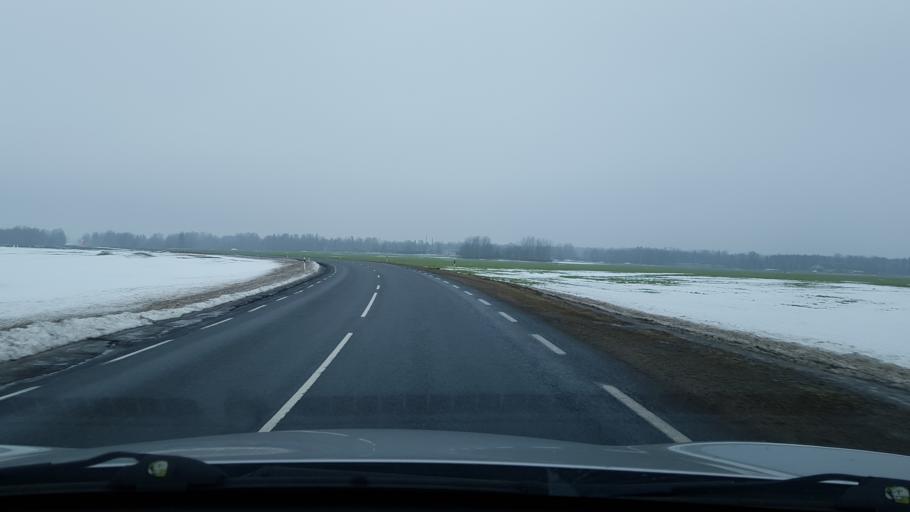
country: EE
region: Valgamaa
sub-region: Torva linn
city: Torva
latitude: 58.2075
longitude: 25.9478
